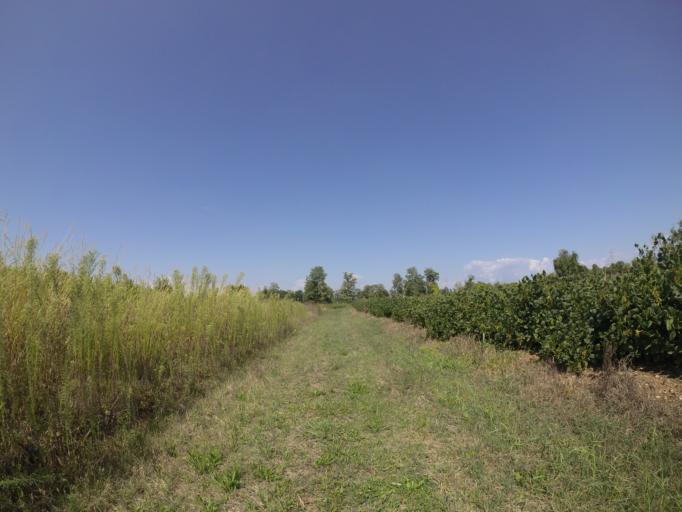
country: IT
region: Friuli Venezia Giulia
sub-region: Provincia di Udine
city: Talmassons
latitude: 45.9431
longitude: 13.0926
